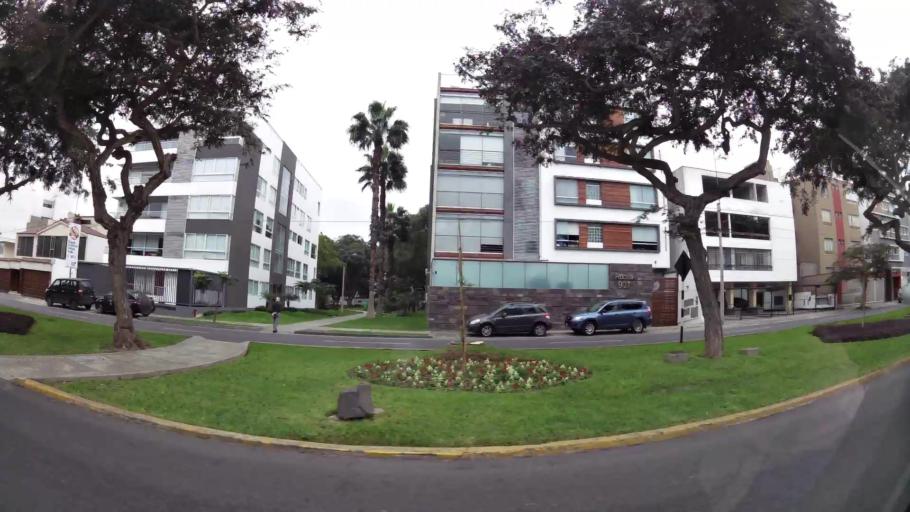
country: PE
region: Lima
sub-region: Lima
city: Surco
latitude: -12.1201
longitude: -77.0123
